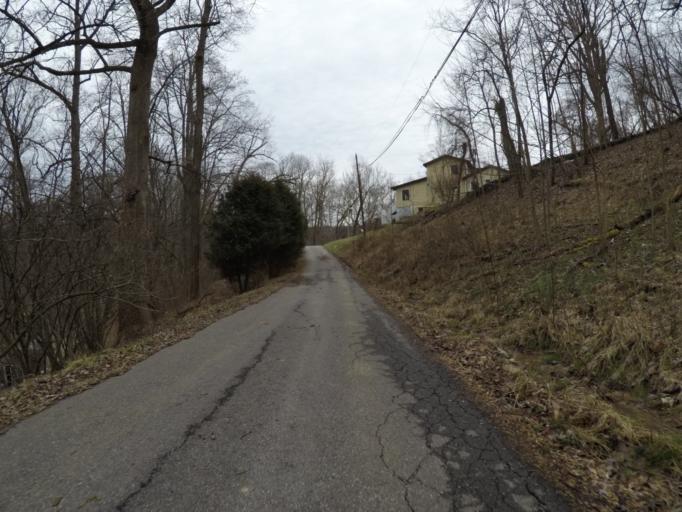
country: US
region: Ohio
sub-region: Lawrence County
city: Burlington
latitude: 38.3904
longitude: -82.5176
